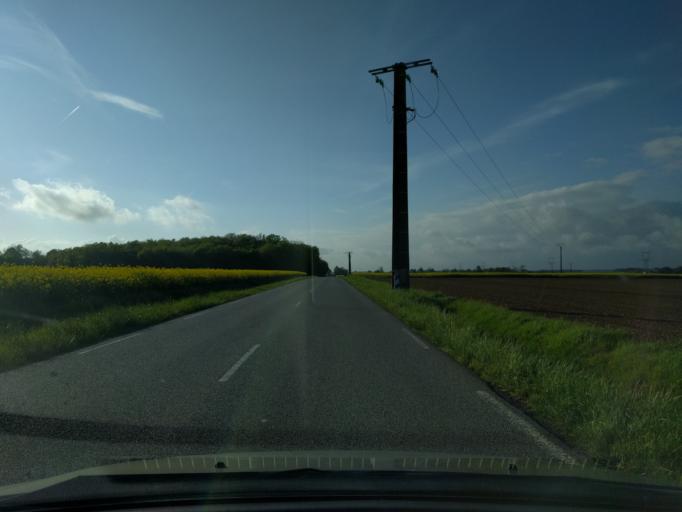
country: FR
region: Haute-Normandie
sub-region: Departement de l'Eure
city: Damville
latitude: 48.8854
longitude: 1.0510
